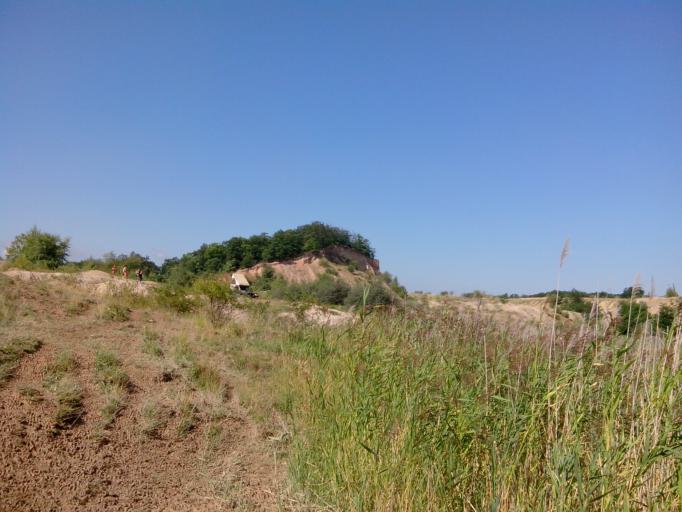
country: RO
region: Cluj
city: Aghiresu-Fabricei
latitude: 46.8895
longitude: 23.2915
